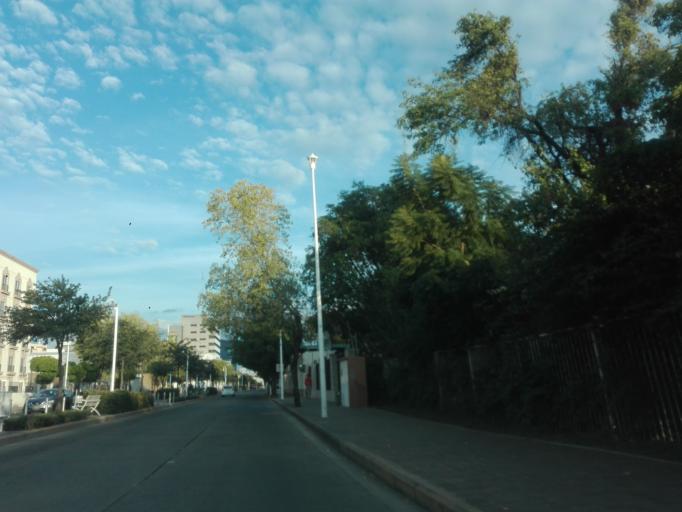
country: MX
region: Guanajuato
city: Leon
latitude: 21.1174
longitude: -101.6640
